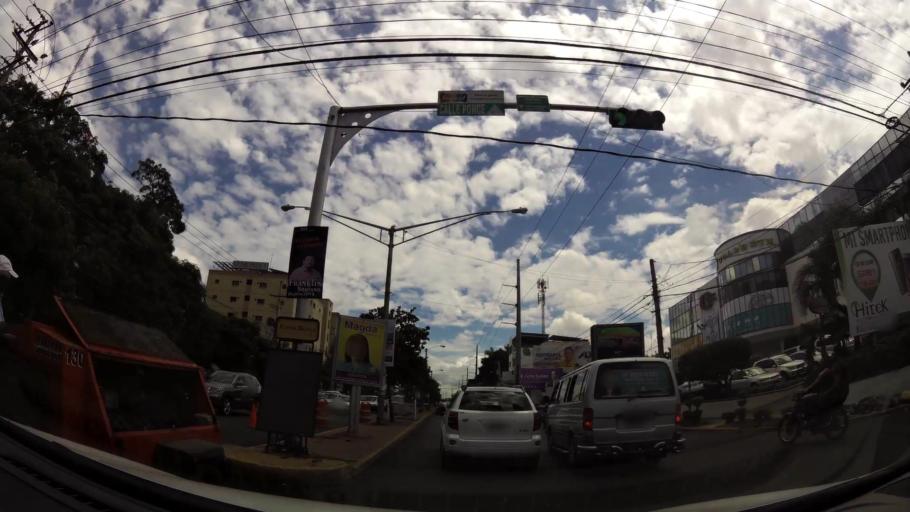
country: DO
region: Santiago
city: Santiago de los Caballeros
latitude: 19.4591
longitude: -70.6813
